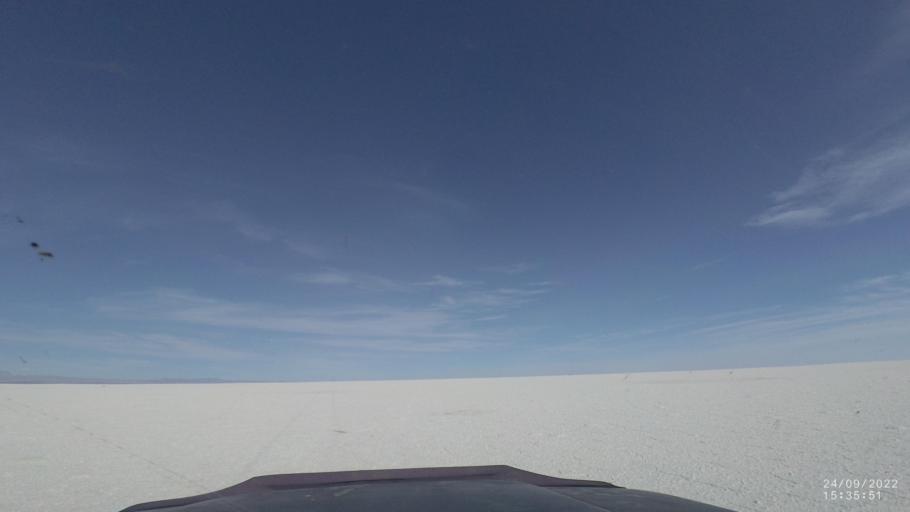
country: BO
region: Potosi
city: Colchani
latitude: -20.1400
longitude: -67.2505
